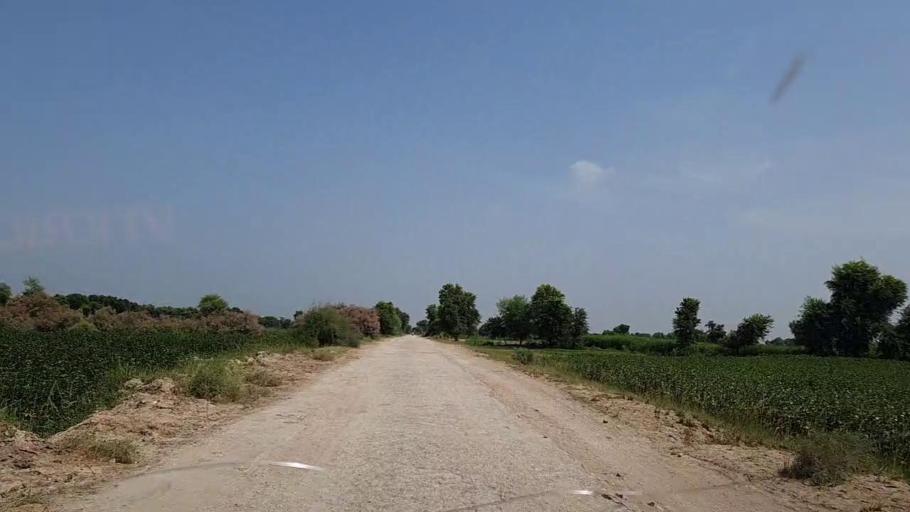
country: PK
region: Sindh
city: Adilpur
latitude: 27.8346
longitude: 69.2855
